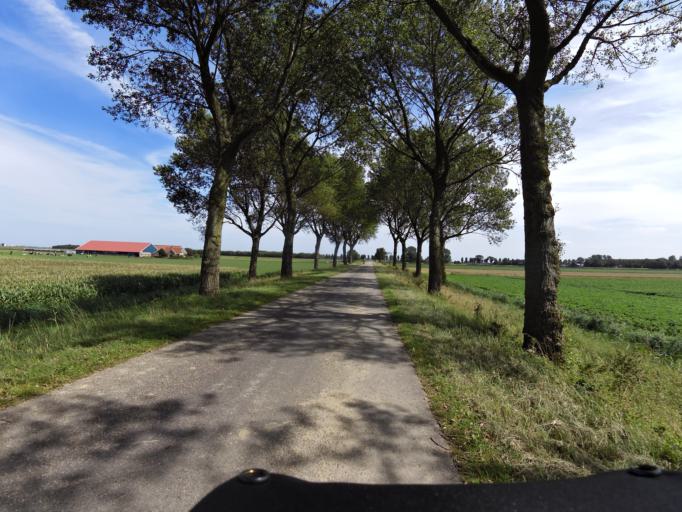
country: NL
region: South Holland
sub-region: Gemeente Goeree-Overflakkee
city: Dirksland
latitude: 51.7853
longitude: 4.1051
